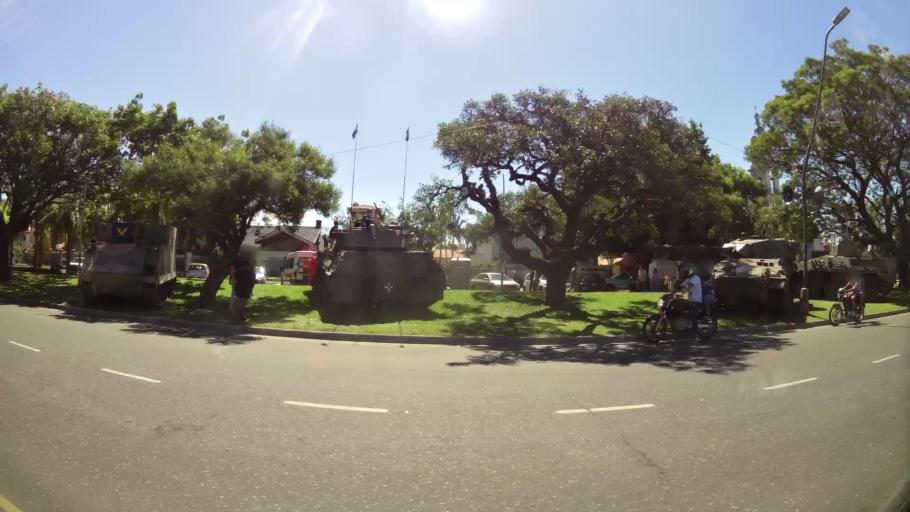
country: AR
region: Santa Fe
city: Santa Fe de la Vera Cruz
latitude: -31.6321
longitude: -60.6792
